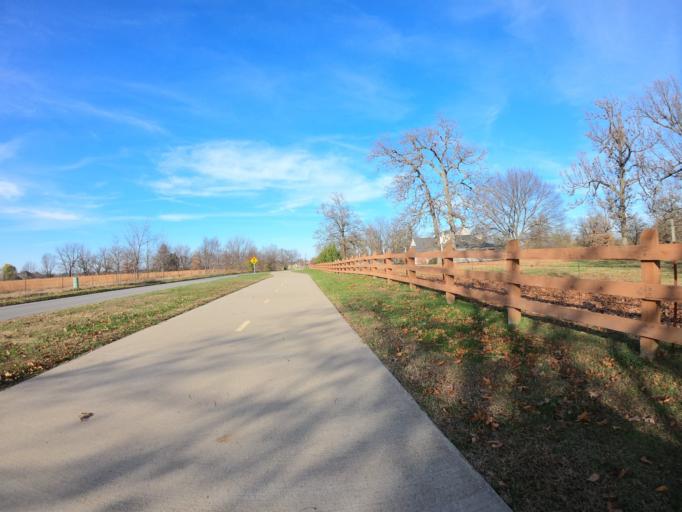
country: US
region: Arkansas
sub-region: Benton County
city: Lowell
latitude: 36.2661
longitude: -94.1634
